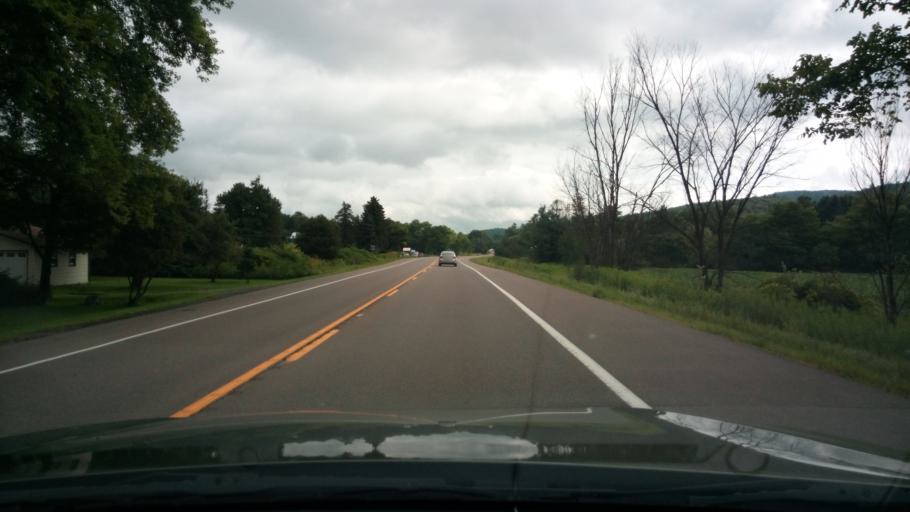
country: US
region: New York
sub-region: Chemung County
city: Horseheads North
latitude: 42.2988
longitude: -76.6853
